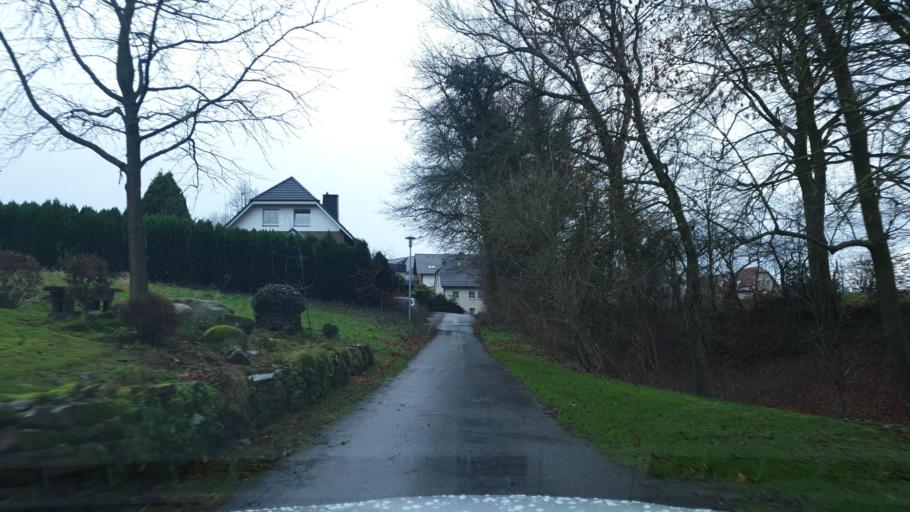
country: DE
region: North Rhine-Westphalia
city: Bad Oeynhausen
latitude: 52.1912
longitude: 8.8325
